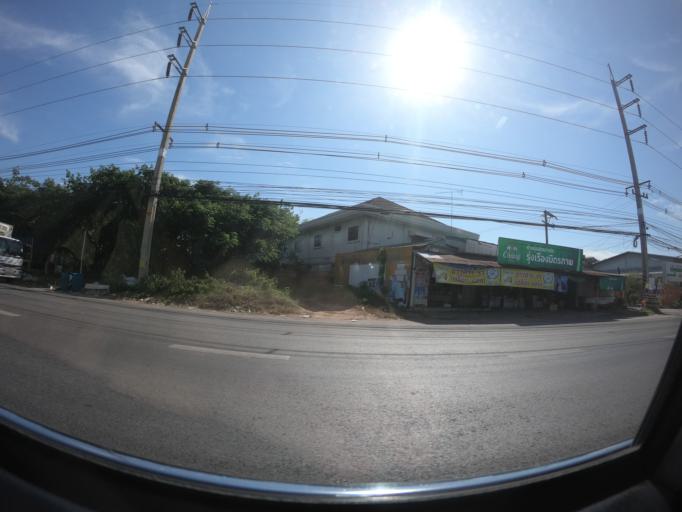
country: TH
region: Khon Kaen
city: Khon Kaen
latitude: 16.3881
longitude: 102.8112
